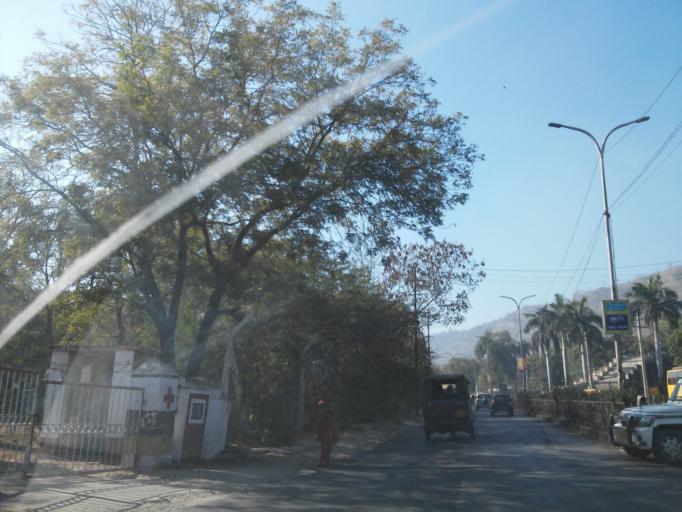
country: IN
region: Rajasthan
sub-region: Udaipur
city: Udaipur
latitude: 24.5654
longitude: 73.6942
